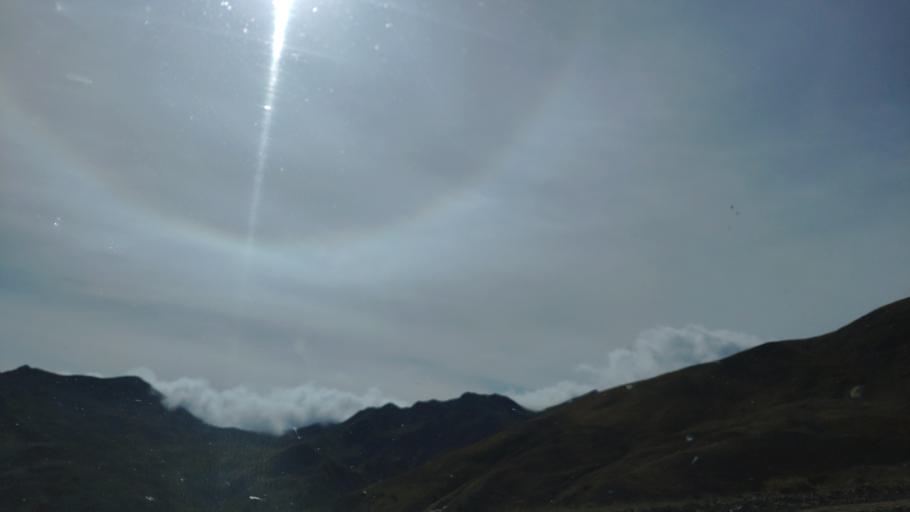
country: AL
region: Korce
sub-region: Rrethi i Kolonjes
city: Erseke
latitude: 40.3721
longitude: 20.8166
